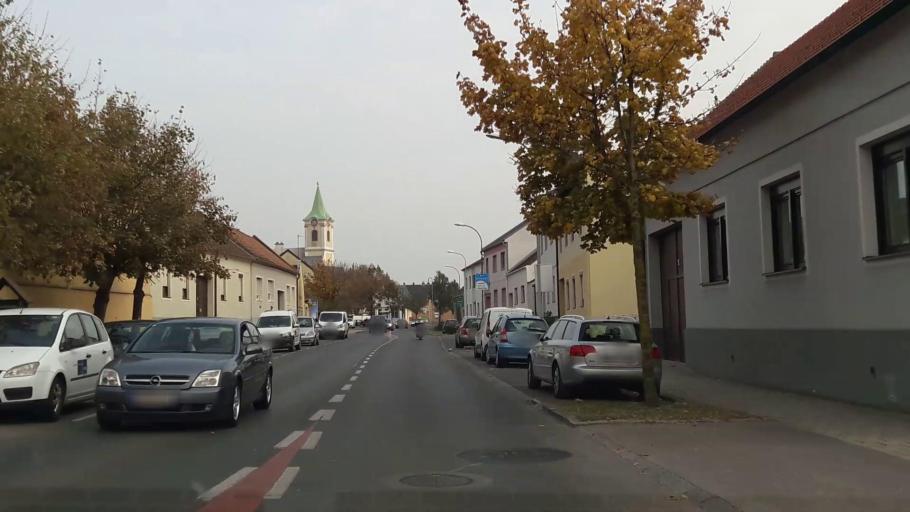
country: AT
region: Burgenland
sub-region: Politischer Bezirk Neusiedl am See
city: Weiden am See
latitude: 47.9287
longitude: 16.8655
